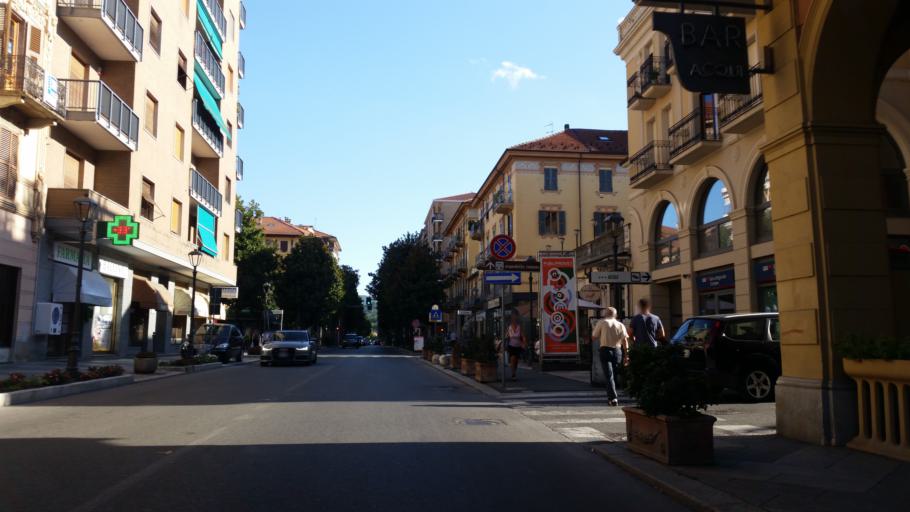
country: IT
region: Piedmont
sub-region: Provincia di Alessandria
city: Acqui Terme
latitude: 44.6720
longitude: 8.4687
